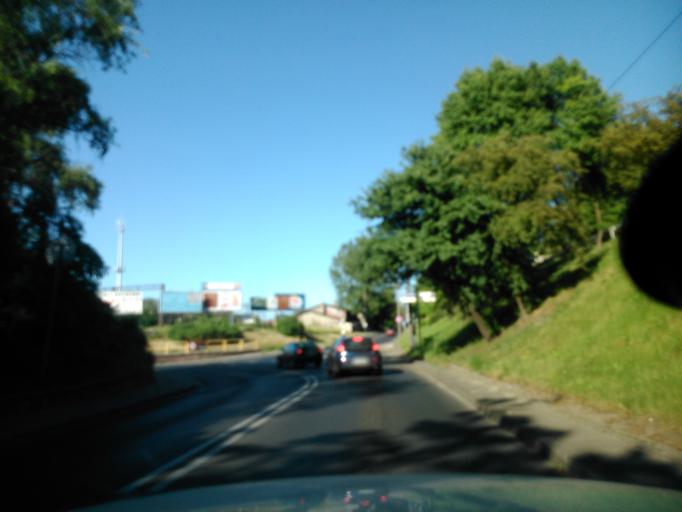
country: PL
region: Kujawsko-Pomorskie
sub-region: Torun
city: Torun
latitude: 52.9971
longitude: 18.6059
